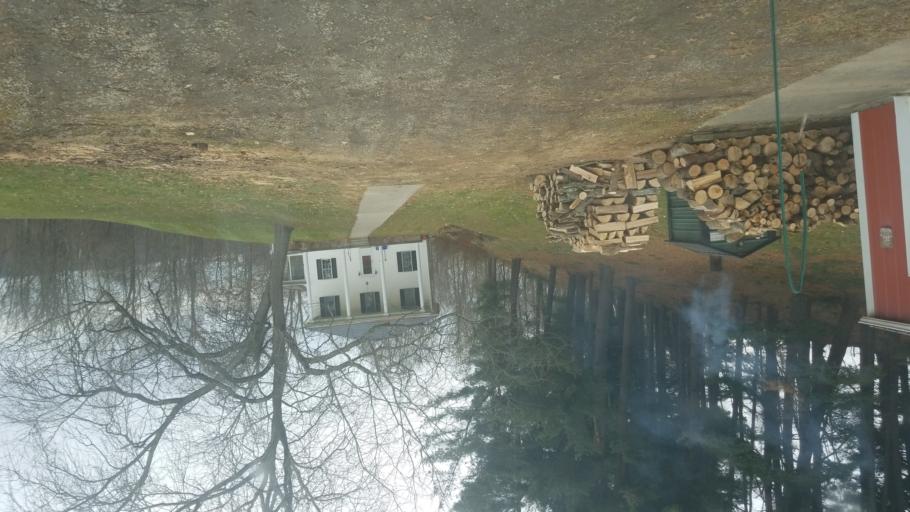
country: US
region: Ohio
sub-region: Richland County
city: Lincoln Heights
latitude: 40.7194
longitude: -82.3771
